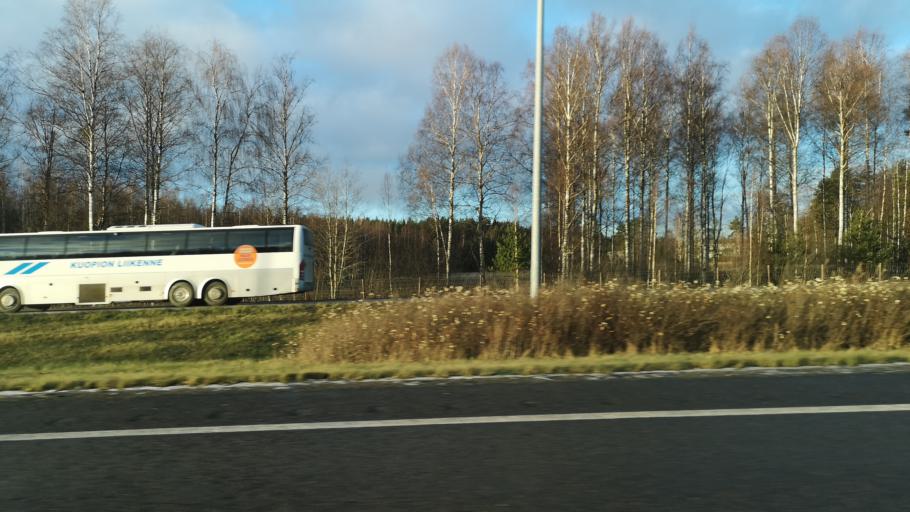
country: FI
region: Paijanne Tavastia
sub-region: Lahti
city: Heinola
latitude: 61.2369
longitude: 26.0456
